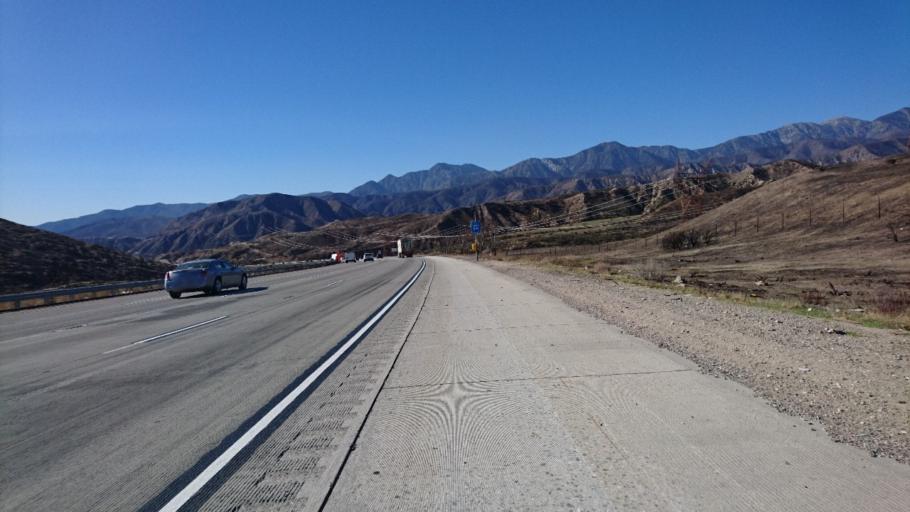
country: US
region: California
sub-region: San Bernardino County
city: Oak Hills
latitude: 34.3443
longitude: -117.4810
